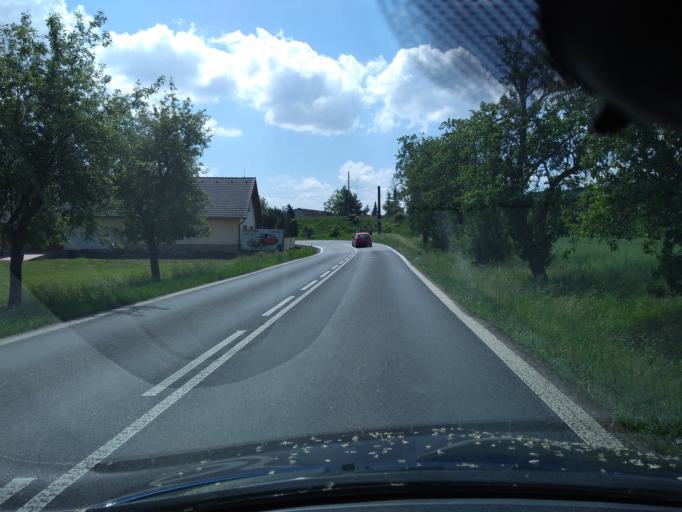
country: CZ
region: Plzensky
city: Svihov
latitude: 49.4499
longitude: 13.2883
